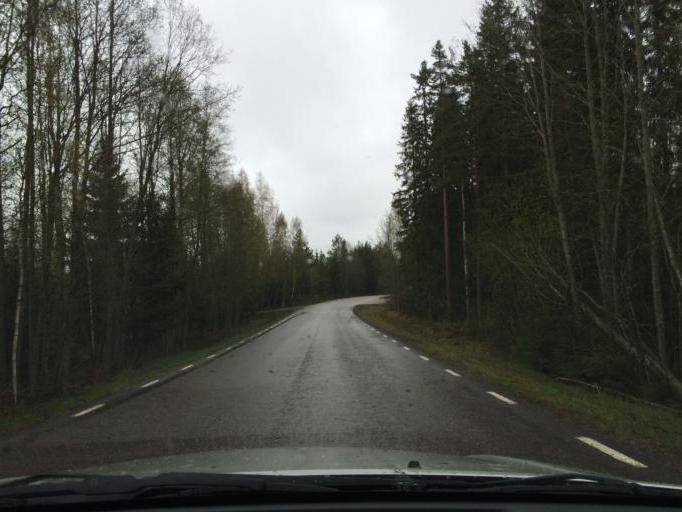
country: SE
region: Dalarna
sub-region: Ludvika Kommun
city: Abborrberget
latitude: 60.0641
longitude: 14.8515
